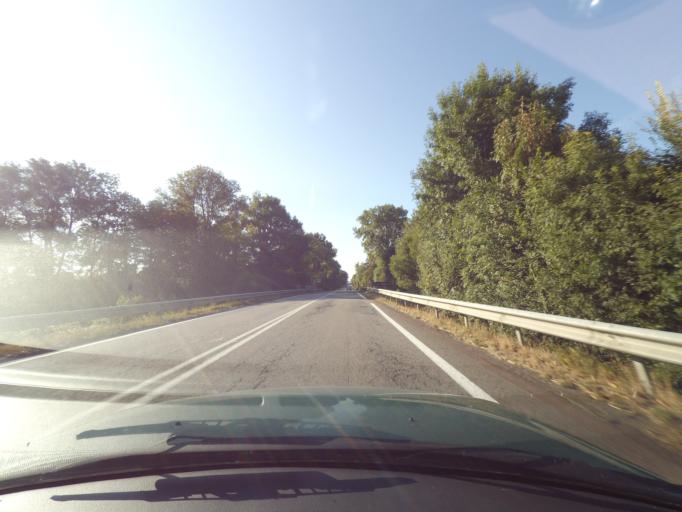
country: FR
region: Poitou-Charentes
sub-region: Departement des Deux-Sevres
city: Viennay
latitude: 46.7075
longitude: -0.2862
